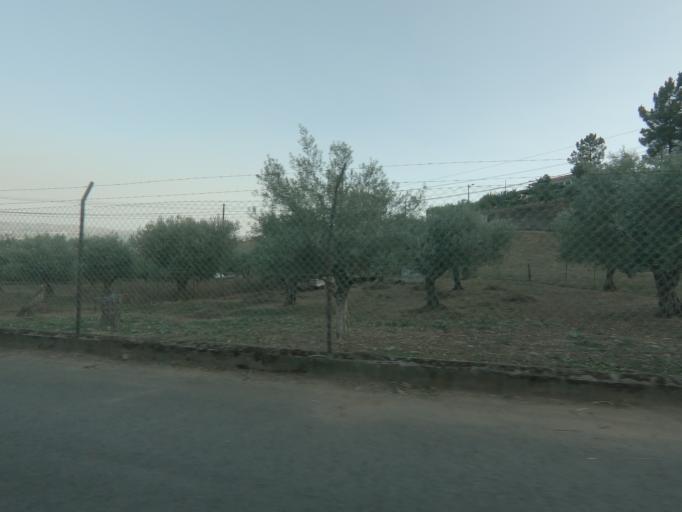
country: PT
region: Vila Real
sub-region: Sabrosa
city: Vilela
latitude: 41.2102
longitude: -7.6678
